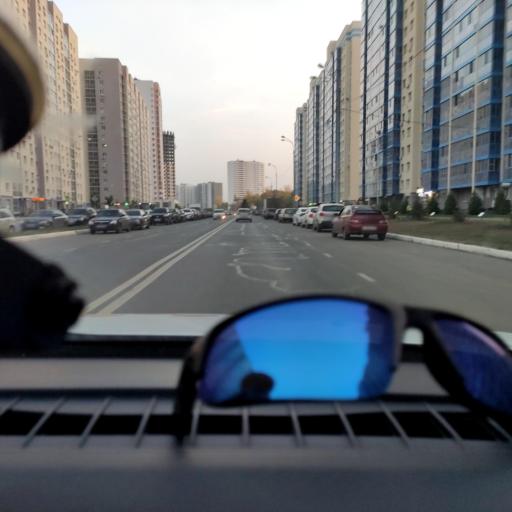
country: RU
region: Samara
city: Rozhdestveno
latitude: 53.1521
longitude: 50.0749
